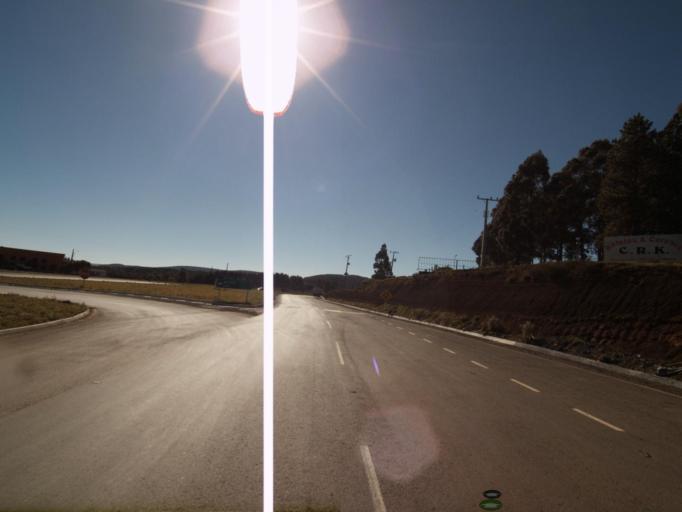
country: BR
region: Parana
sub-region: Palmas
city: Palmas
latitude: -26.6843
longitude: -51.5646
